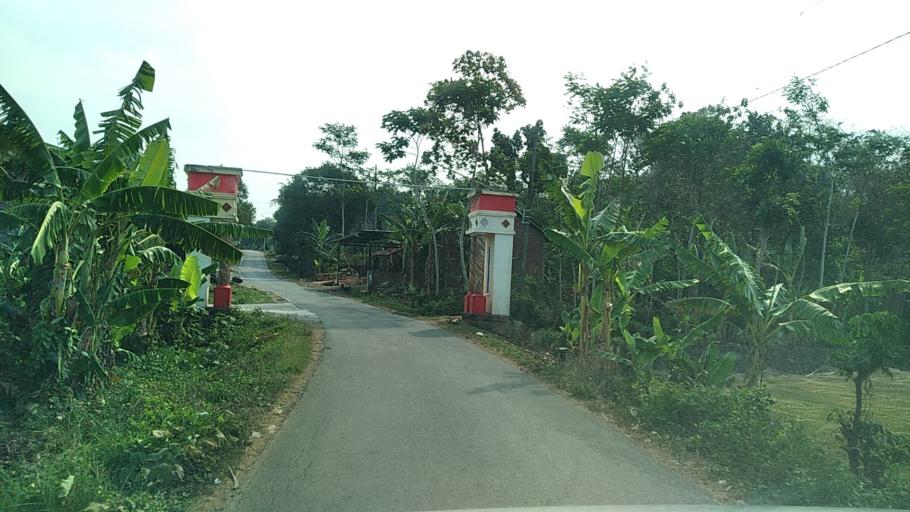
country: ID
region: Central Java
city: Ungaran
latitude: -7.0581
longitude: 110.3039
